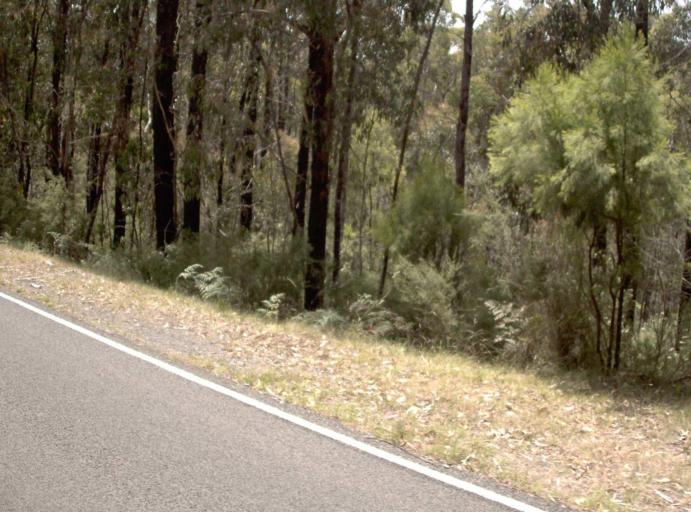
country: AU
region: Victoria
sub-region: Latrobe
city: Moe
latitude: -38.0297
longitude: 146.3515
